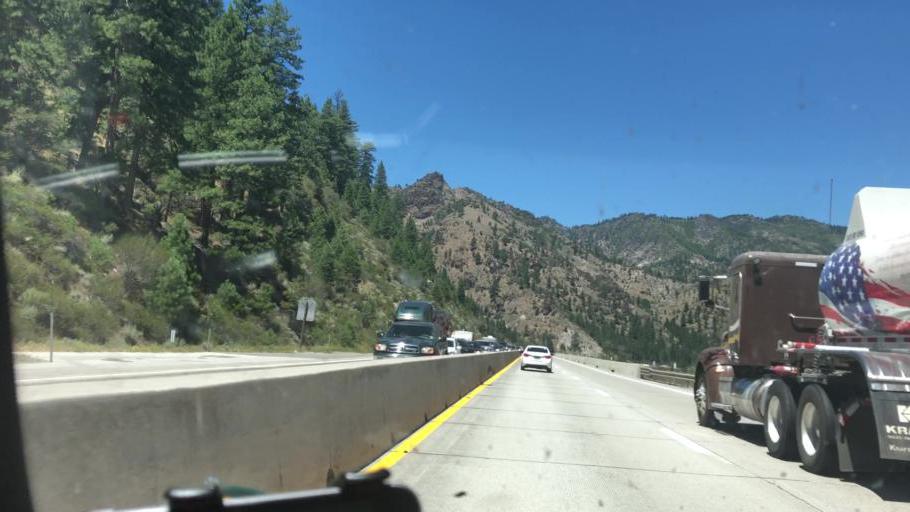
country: US
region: Nevada
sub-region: Washoe County
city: Verdi
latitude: 39.4164
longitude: -120.0298
